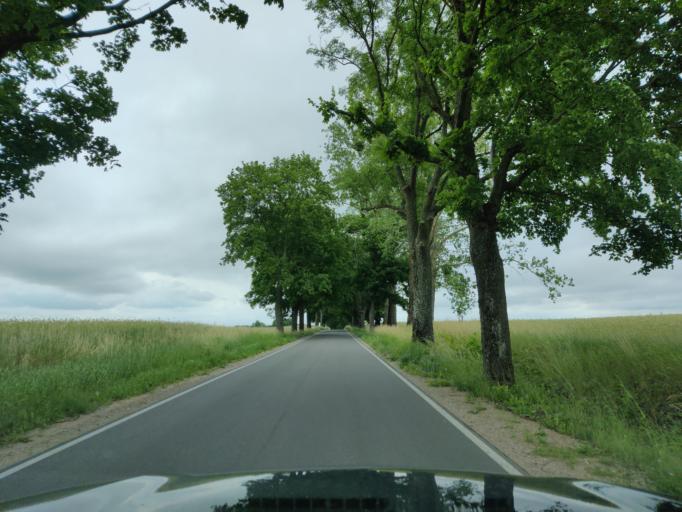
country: PL
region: Warmian-Masurian Voivodeship
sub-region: Powiat mragowski
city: Mikolajki
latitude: 53.8612
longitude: 21.6045
